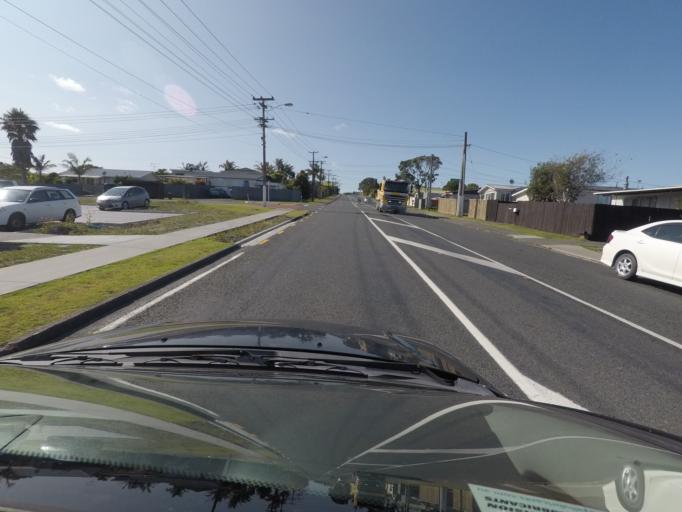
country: NZ
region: Auckland
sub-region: Auckland
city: Warkworth
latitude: -36.4242
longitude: 174.7275
